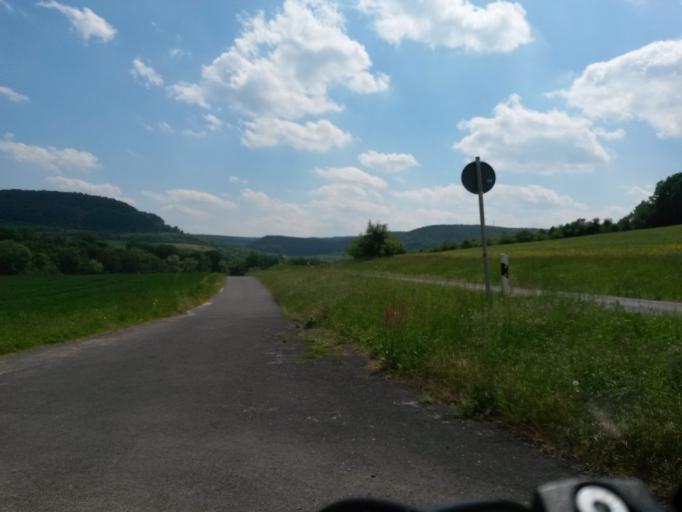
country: DE
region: Bavaria
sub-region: Regierungsbezirk Unterfranken
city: Euerdorf
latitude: 50.1584
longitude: 10.0195
